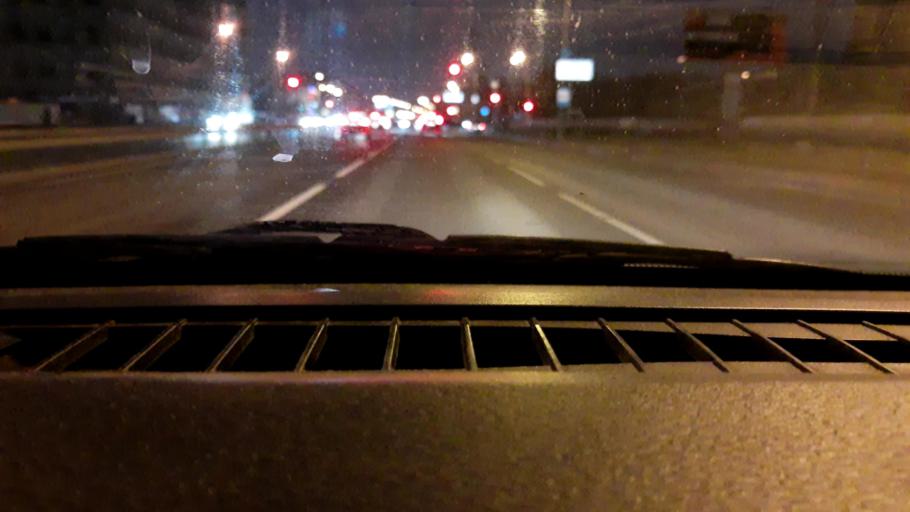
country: RU
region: Nizjnij Novgorod
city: Nizhniy Novgorod
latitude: 56.2644
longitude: 43.9224
